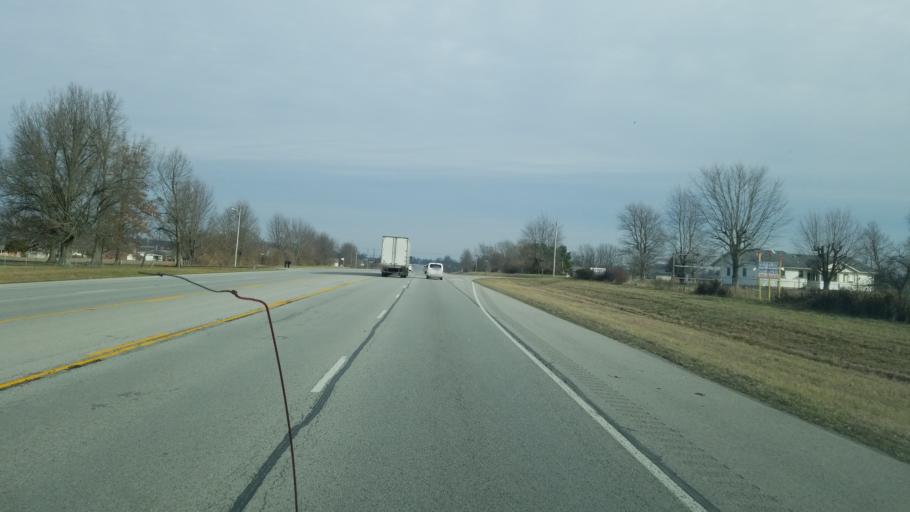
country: US
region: Kentucky
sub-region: Boyle County
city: Junction City
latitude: 37.5865
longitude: -84.7836
